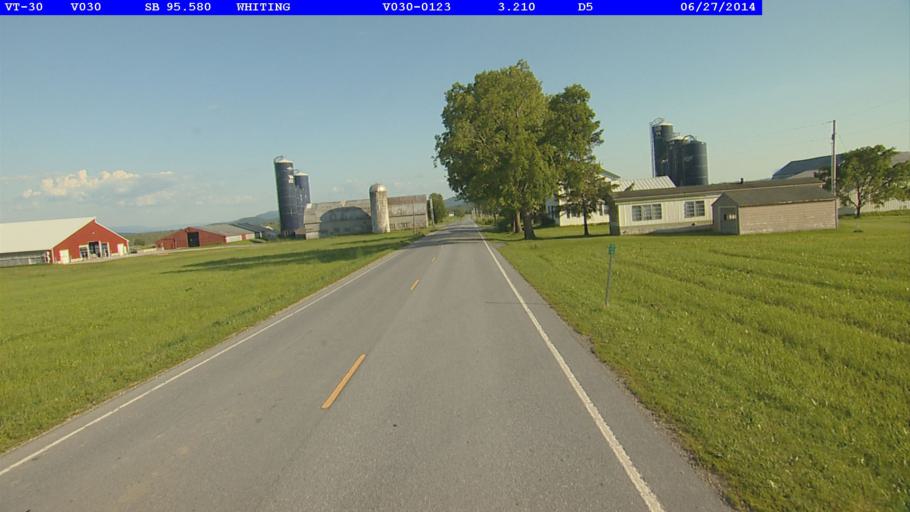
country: US
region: Vermont
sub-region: Addison County
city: Middlebury (village)
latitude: 43.8836
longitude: -73.2009
